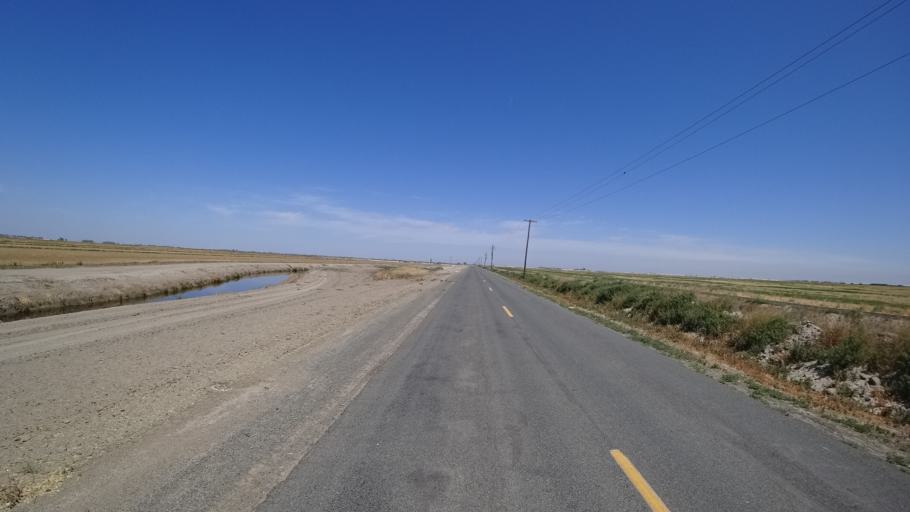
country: US
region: California
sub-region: Kings County
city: Stratford
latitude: 36.1704
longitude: -119.7175
